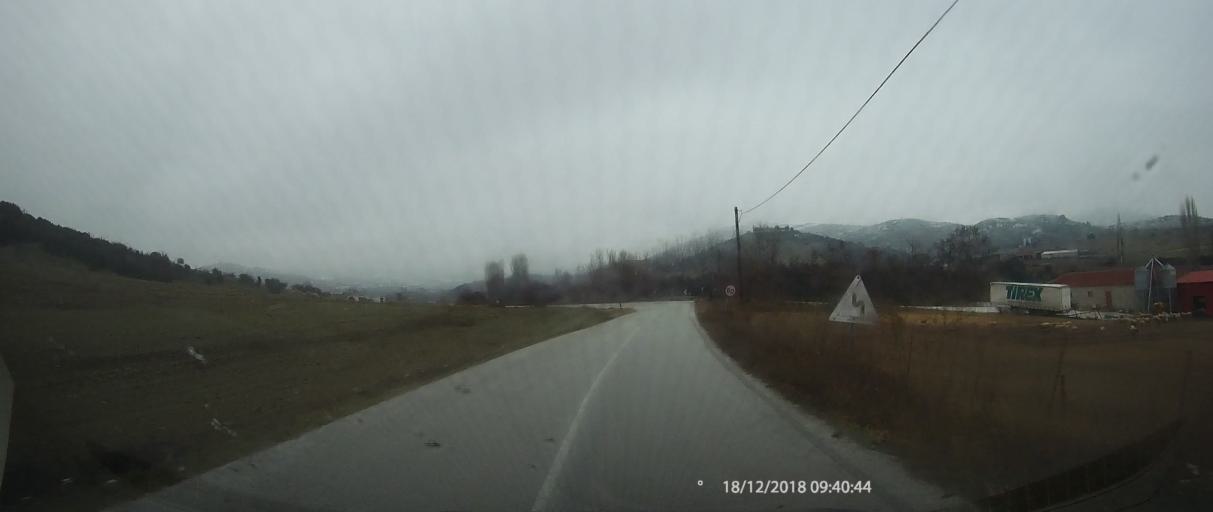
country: GR
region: Thessaly
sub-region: Nomos Larisis
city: Elassona
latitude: 40.0058
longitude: 22.2294
